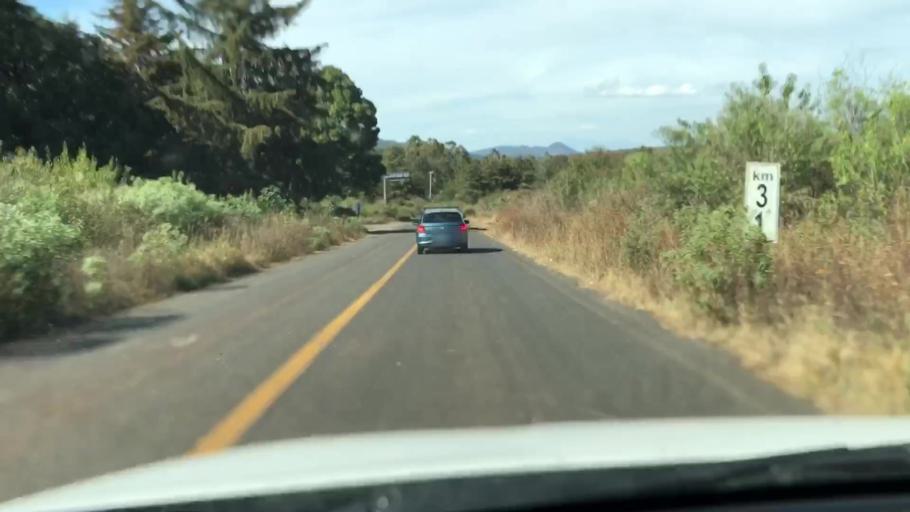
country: MX
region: Jalisco
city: Chiquilistlan
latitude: 20.1469
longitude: -103.7250
